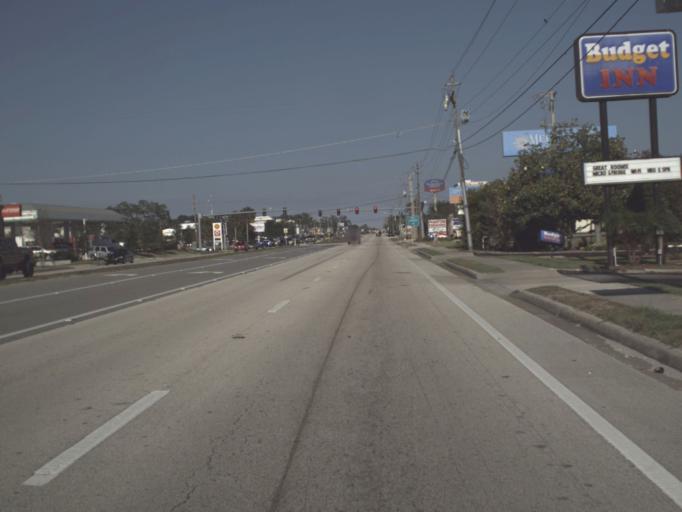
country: US
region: Florida
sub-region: Brevard County
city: June Park
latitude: 28.0788
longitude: -80.7021
